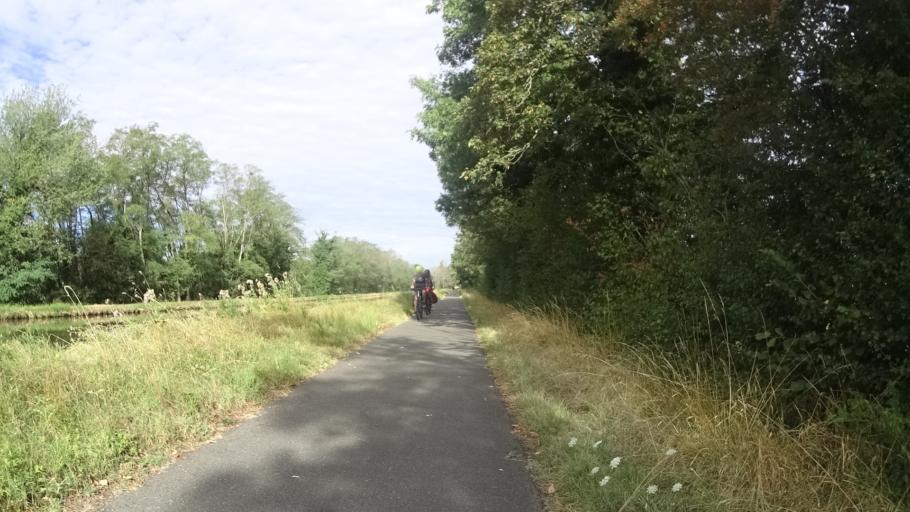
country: FR
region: Auvergne
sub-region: Departement de l'Allier
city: Diou
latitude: 46.5191
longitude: 3.7850
